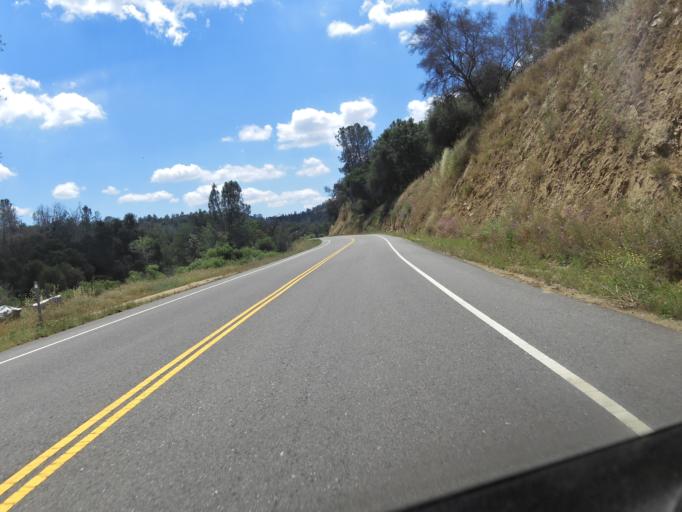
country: US
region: California
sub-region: Madera County
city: Coarsegold
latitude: 37.1648
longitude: -119.6408
